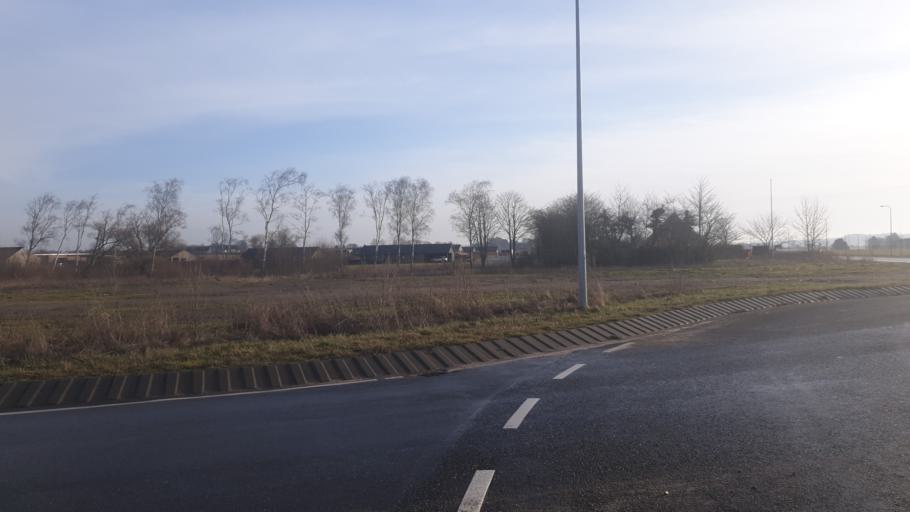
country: DK
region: Central Jutland
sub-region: Hedensted Kommune
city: Hedensted
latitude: 55.7634
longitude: 9.7243
